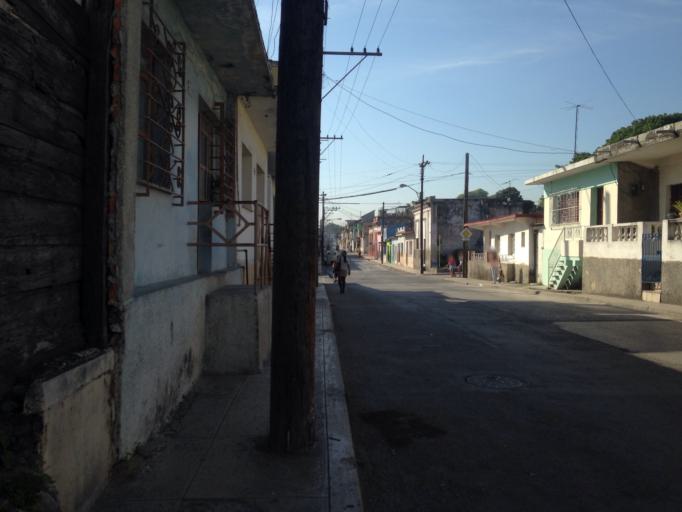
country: CU
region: La Habana
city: Regla
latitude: 23.1257
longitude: -82.3328
